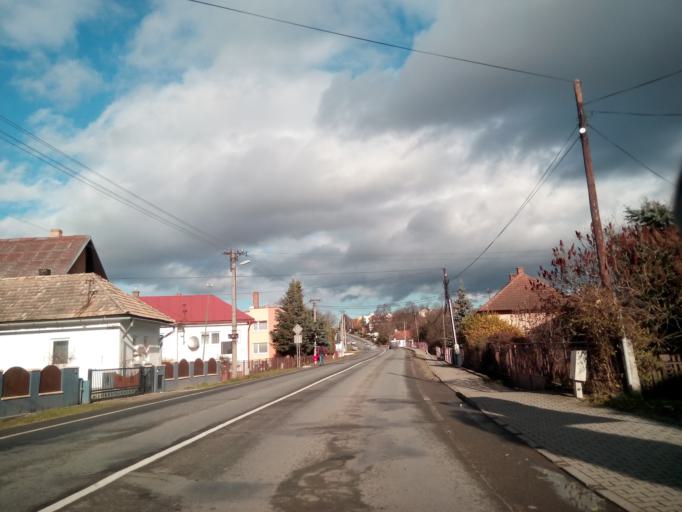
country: SK
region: Presovsky
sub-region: Okres Bardejov
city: Bardejov
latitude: 49.1512
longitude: 21.3147
